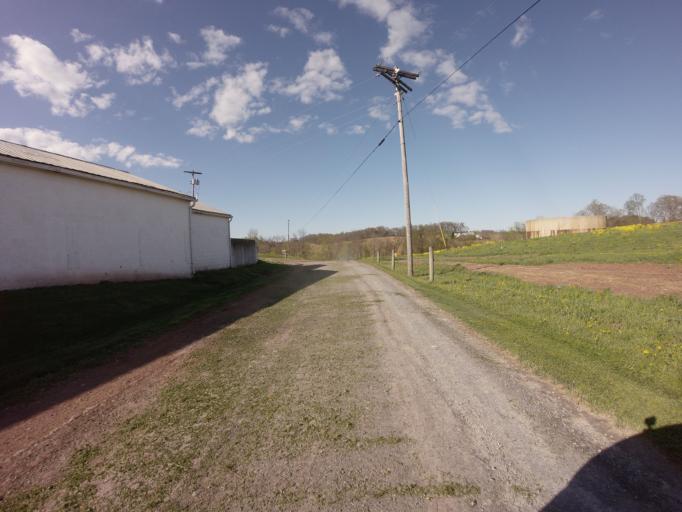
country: US
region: Maryland
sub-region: Carroll County
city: Taneytown
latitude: 39.6090
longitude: -77.2523
